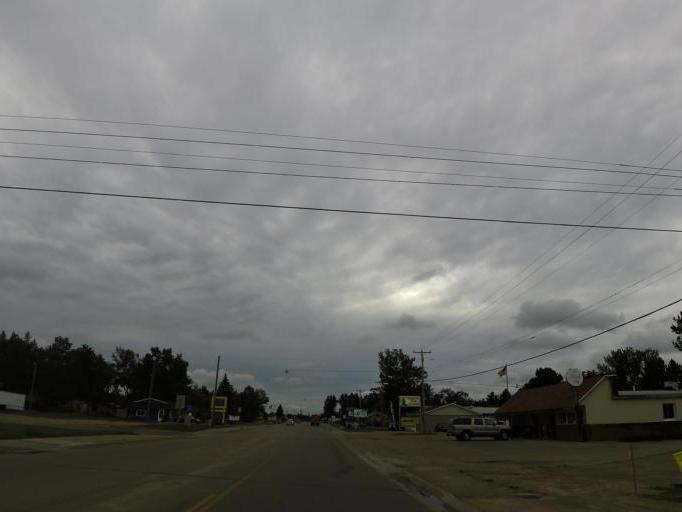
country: US
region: Michigan
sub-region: Roscommon County
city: Saint Helen
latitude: 44.3582
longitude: -84.4103
